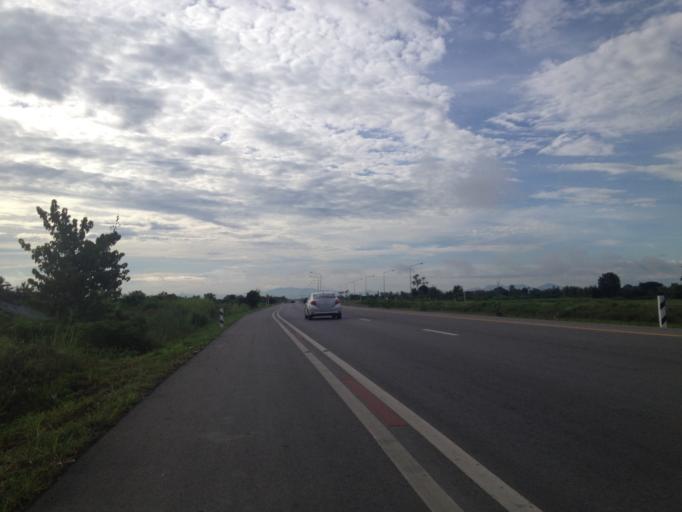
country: TH
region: Chiang Mai
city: San Pa Tong
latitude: 18.5900
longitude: 98.8376
